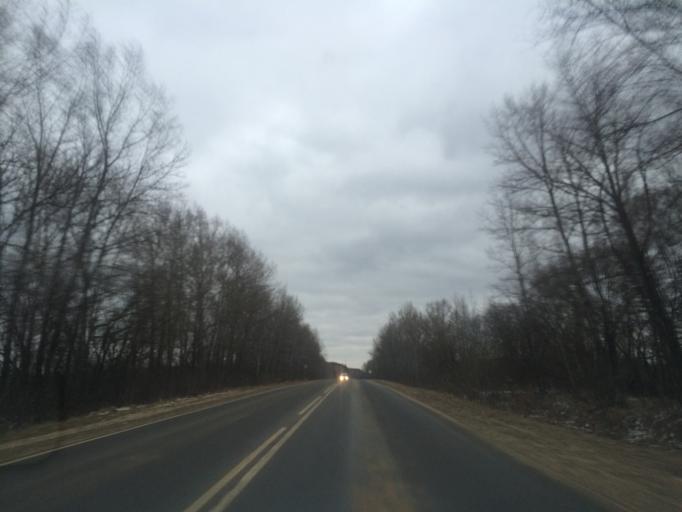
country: RU
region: Tula
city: Odoyev
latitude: 53.9851
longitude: 36.7191
